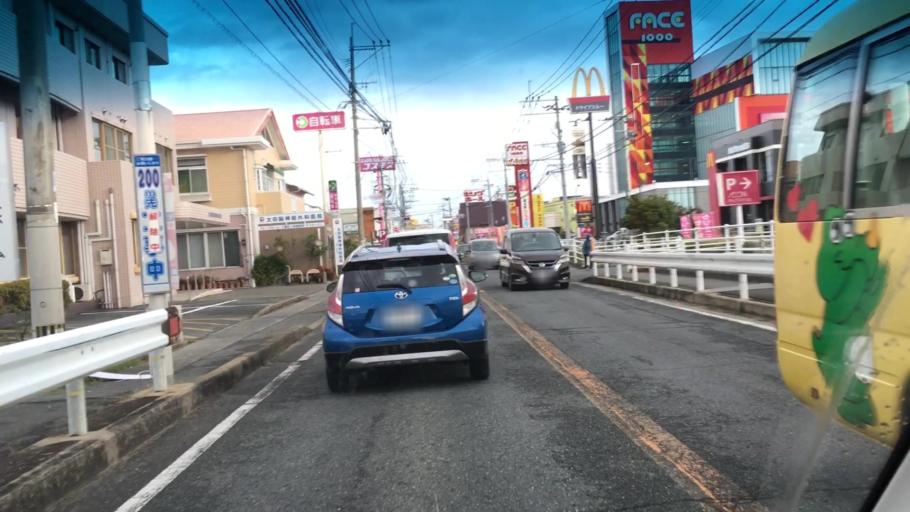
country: JP
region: Fukuoka
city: Maebaru-chuo
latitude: 33.5615
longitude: 130.2099
